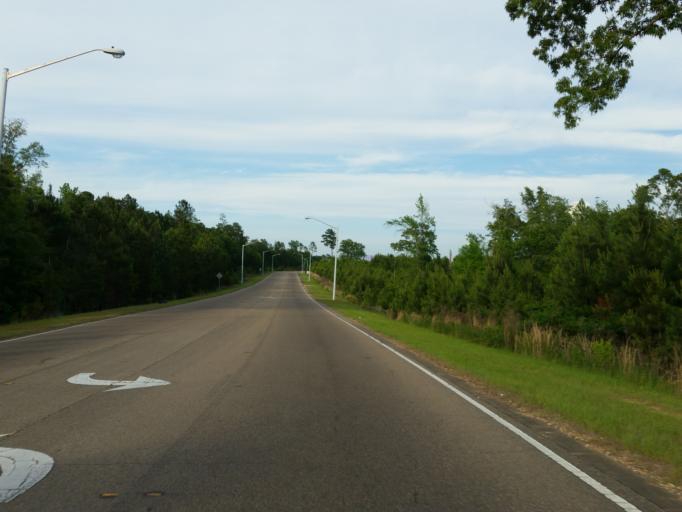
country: US
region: Mississippi
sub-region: Lamar County
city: West Hattiesburg
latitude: 31.2992
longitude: -89.3707
